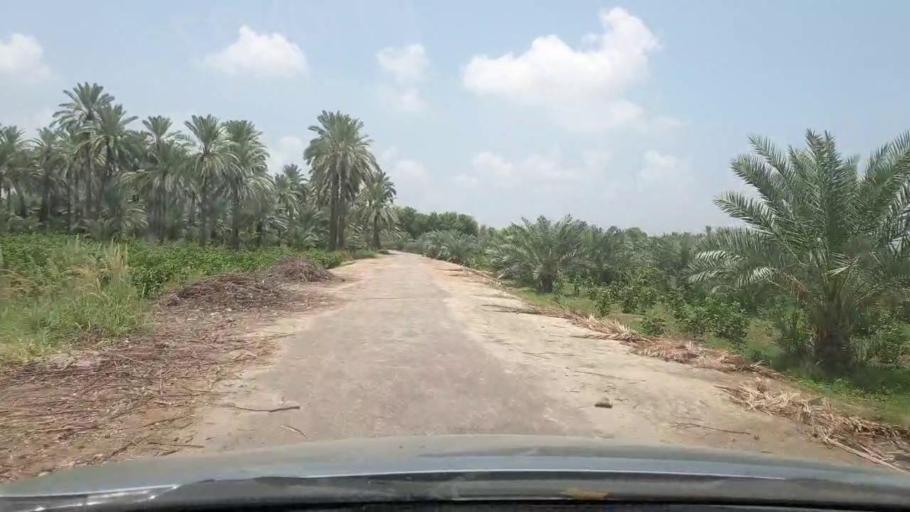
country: PK
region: Sindh
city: Khairpur
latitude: 27.4748
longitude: 68.7308
